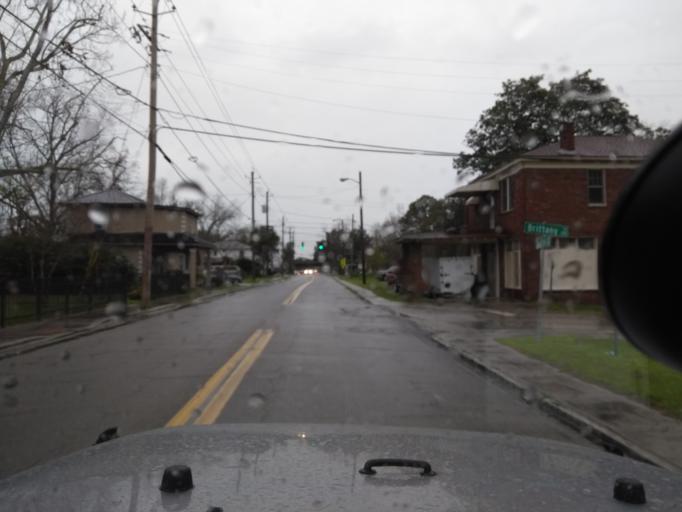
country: US
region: Georgia
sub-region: Chatham County
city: Savannah
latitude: 32.0873
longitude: -81.1249
